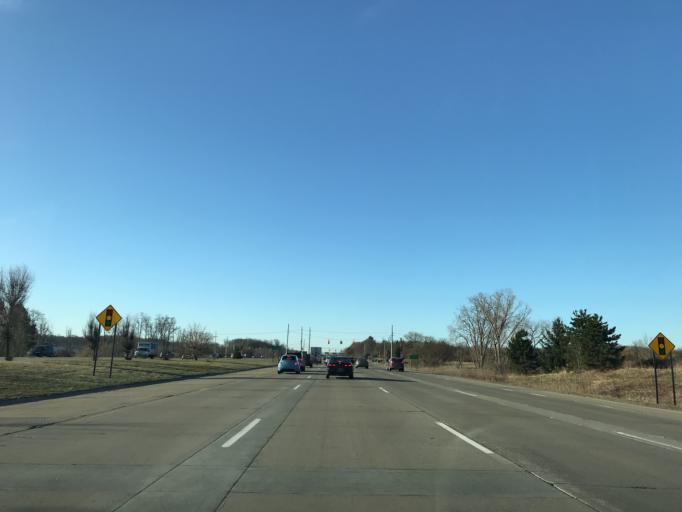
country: US
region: Michigan
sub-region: Oakland County
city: Walled Lake
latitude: 42.5143
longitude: -83.4467
